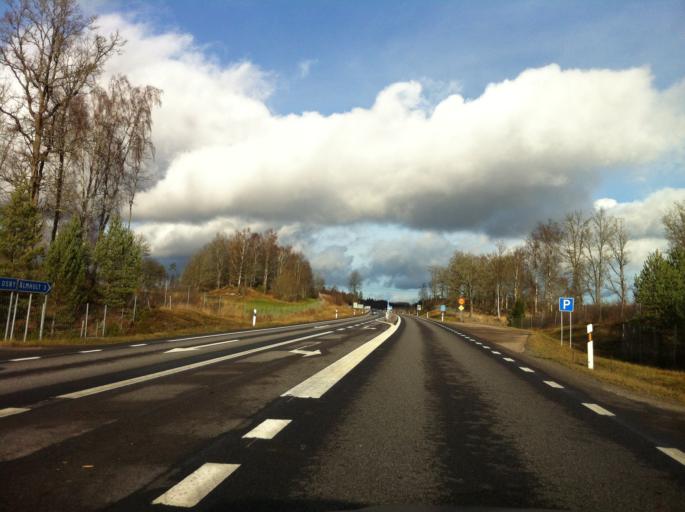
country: SE
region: Kronoberg
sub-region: Almhults Kommun
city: AElmhult
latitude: 56.5067
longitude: 14.1267
